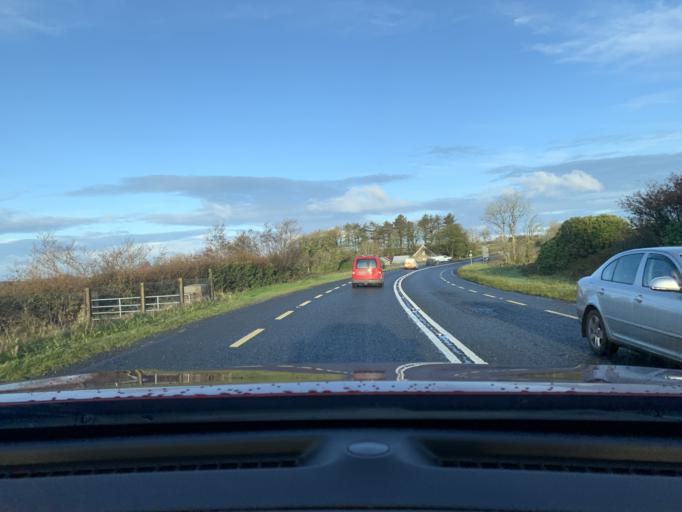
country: IE
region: Connaught
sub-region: Sligo
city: Sligo
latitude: 54.3615
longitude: -8.5253
